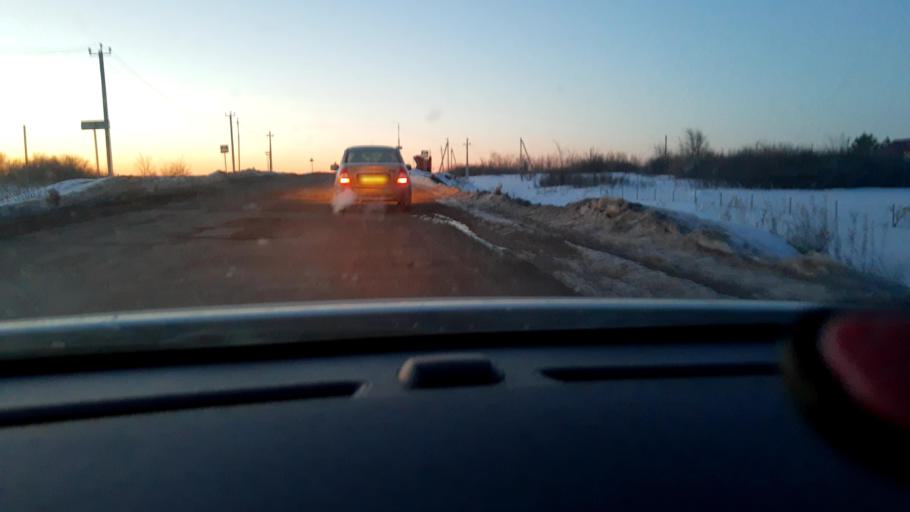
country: RU
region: Bashkortostan
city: Avdon
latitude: 54.3968
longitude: 55.7024
